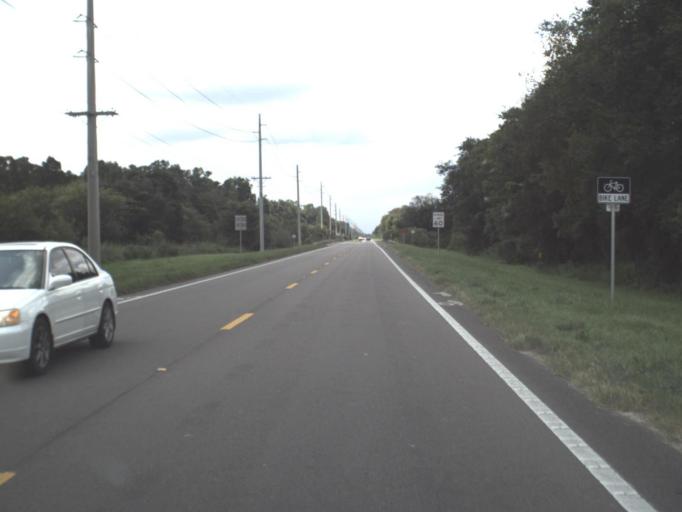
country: US
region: Florida
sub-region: Pasco County
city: Crystal Springs
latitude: 28.1376
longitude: -82.1495
